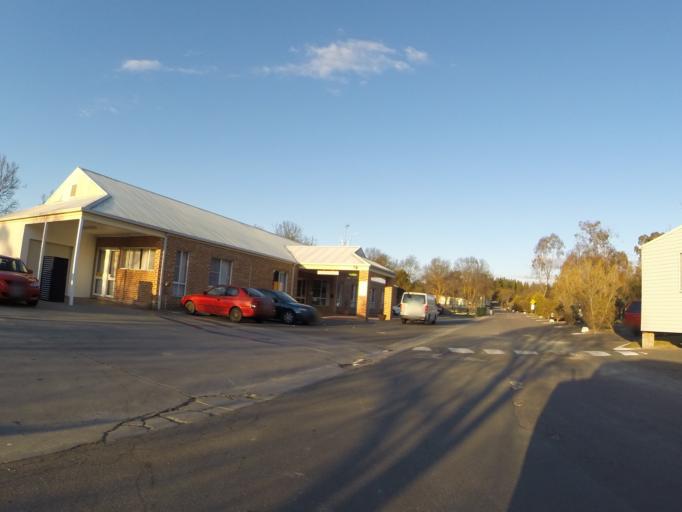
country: AU
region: Australian Capital Territory
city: Kaleen
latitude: -35.1985
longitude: 149.2248
